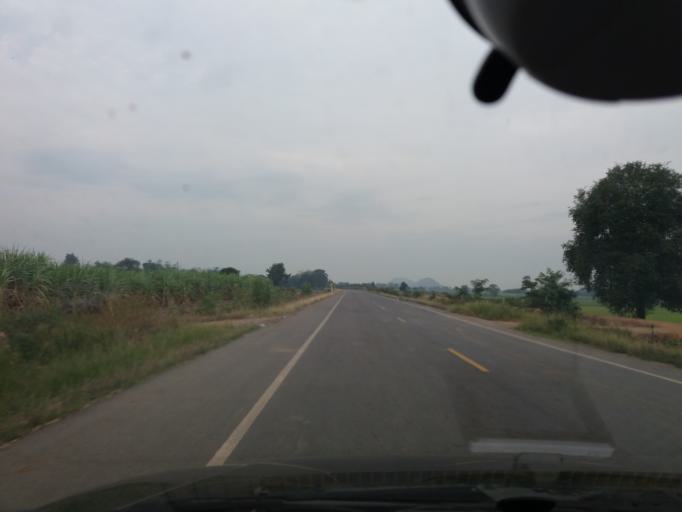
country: TH
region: Suphan Buri
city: Doem Bang Nang Buat
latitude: 14.8620
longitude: 100.1294
